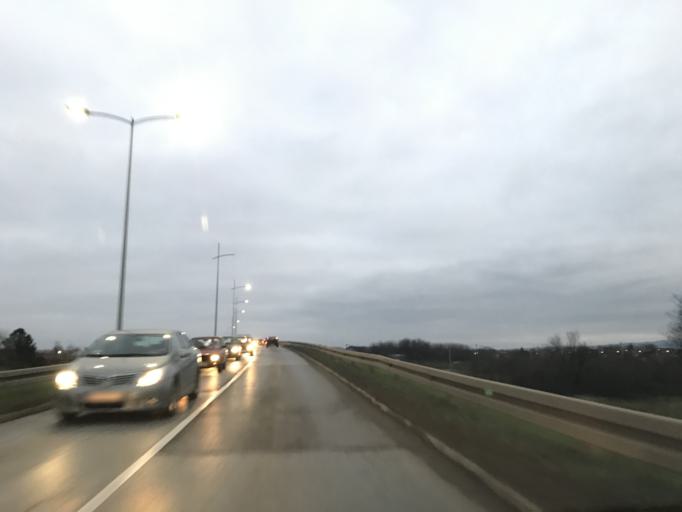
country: RS
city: Veternik
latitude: 45.2818
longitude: 19.7777
